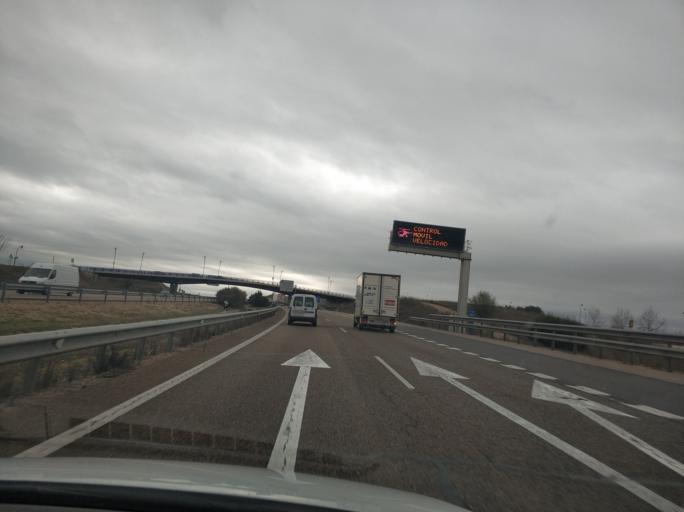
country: ES
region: Castille and Leon
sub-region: Provincia de Valladolid
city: Arroyo
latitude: 41.6222
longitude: -4.7895
